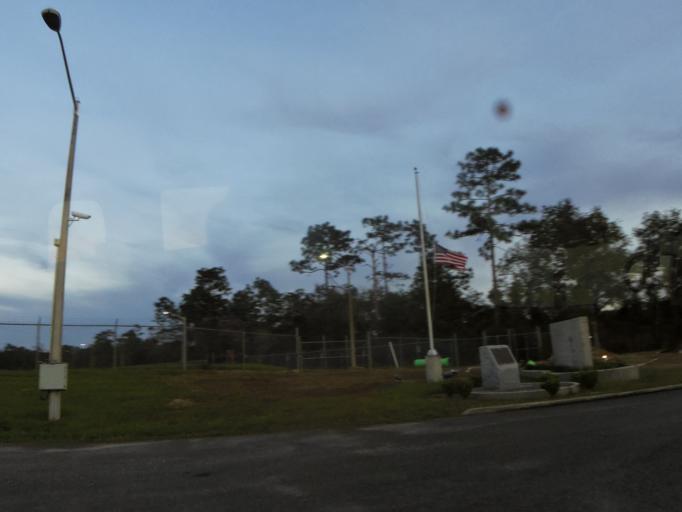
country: US
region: Florida
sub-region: Saint Johns County
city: Fruit Cove
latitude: 30.1558
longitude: -81.5193
